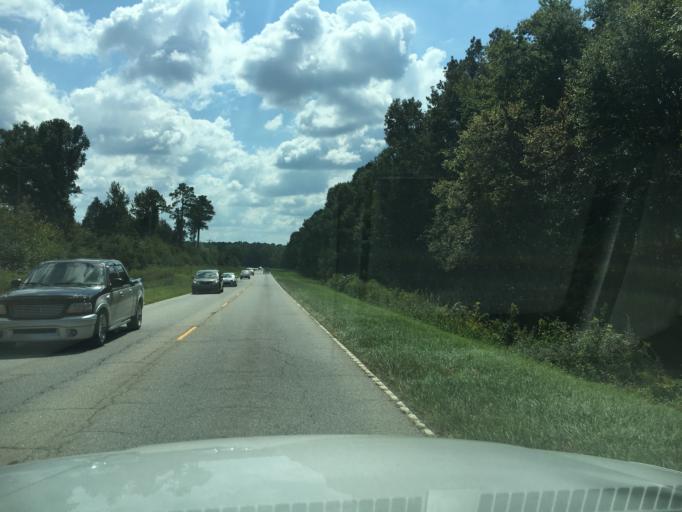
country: US
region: South Carolina
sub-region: Greenwood County
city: Greenwood
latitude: 34.1701
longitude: -82.1829
